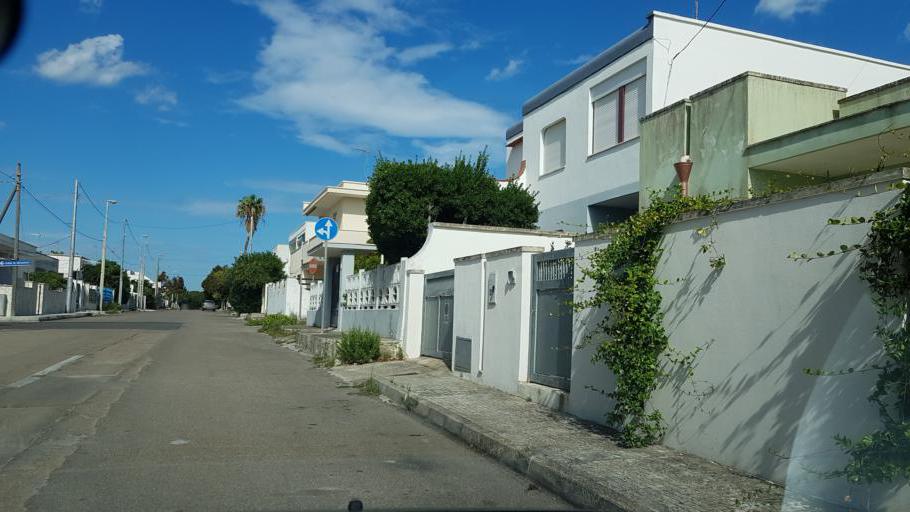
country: IT
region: Apulia
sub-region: Provincia di Lecce
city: Borgagne
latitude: 40.2746
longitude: 18.4264
